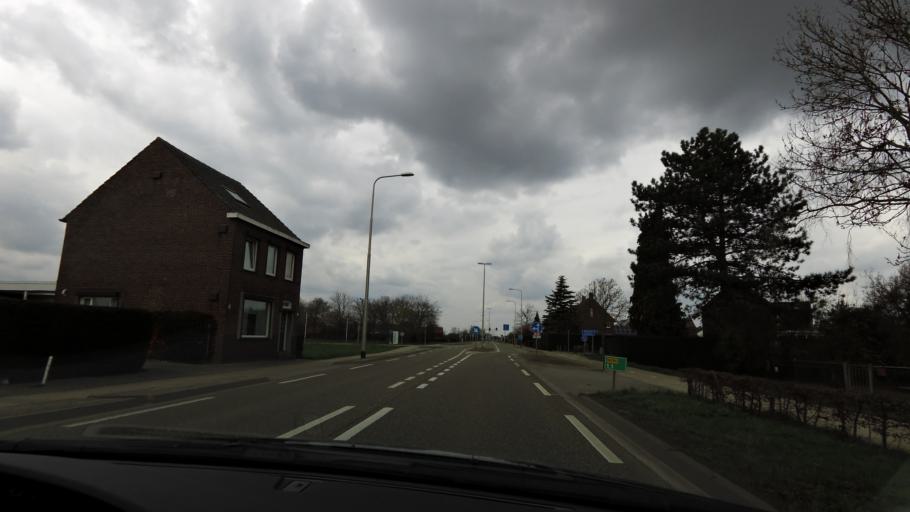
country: NL
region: Limburg
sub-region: Gemeente Sittard-Geleen
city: Born
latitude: 51.0717
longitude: 5.8437
